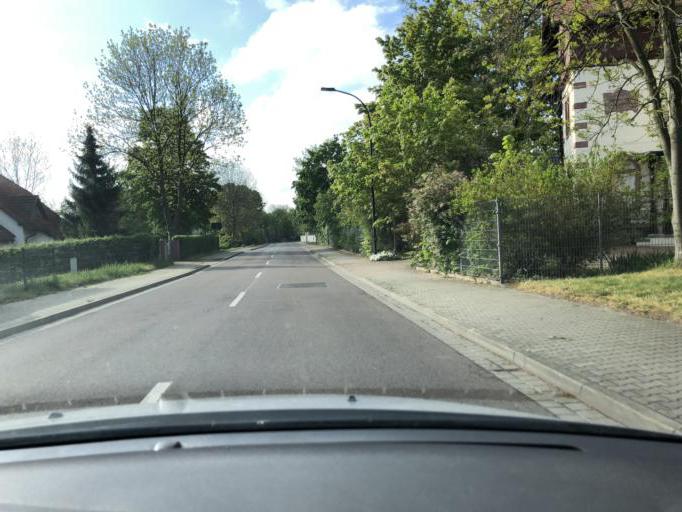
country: DE
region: Saxony
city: Markkleeberg
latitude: 51.2453
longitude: 12.3833
